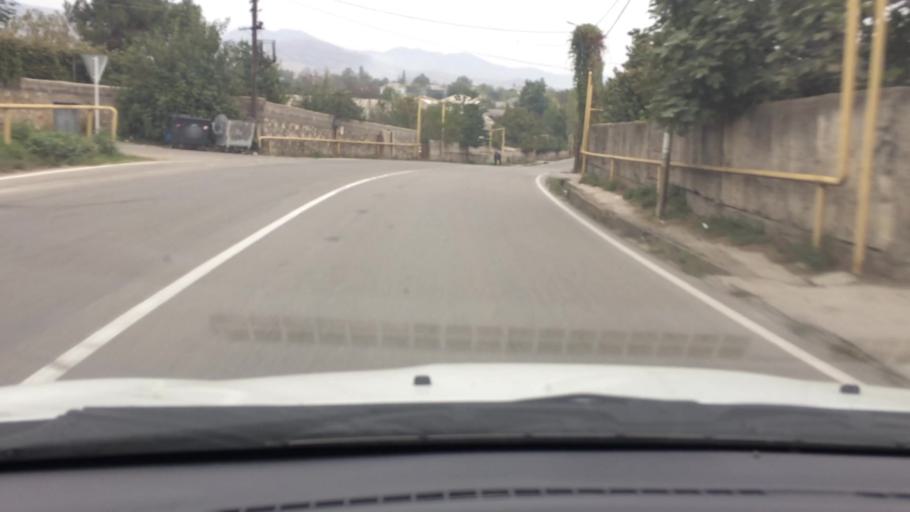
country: AM
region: Tavush
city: Bagratashen
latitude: 41.2428
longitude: 44.7985
